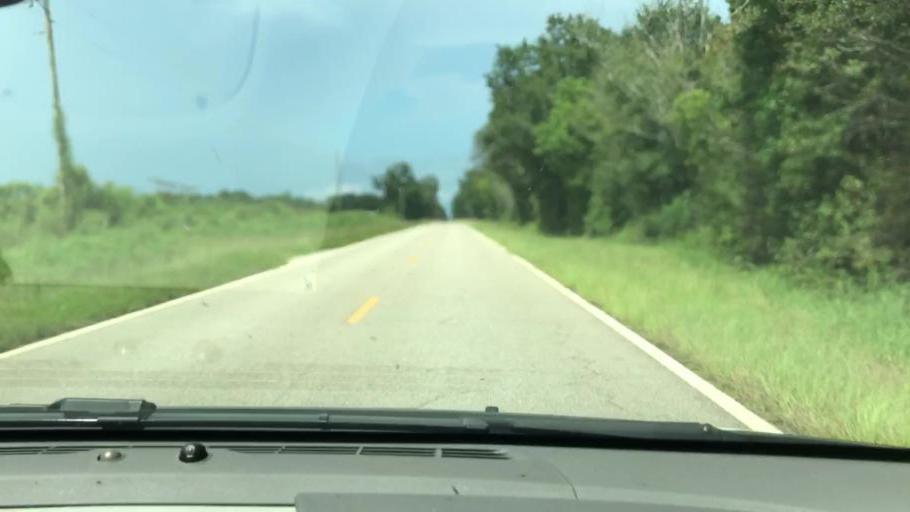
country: US
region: Georgia
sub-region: Seminole County
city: Donalsonville
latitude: 31.1307
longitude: -84.9953
